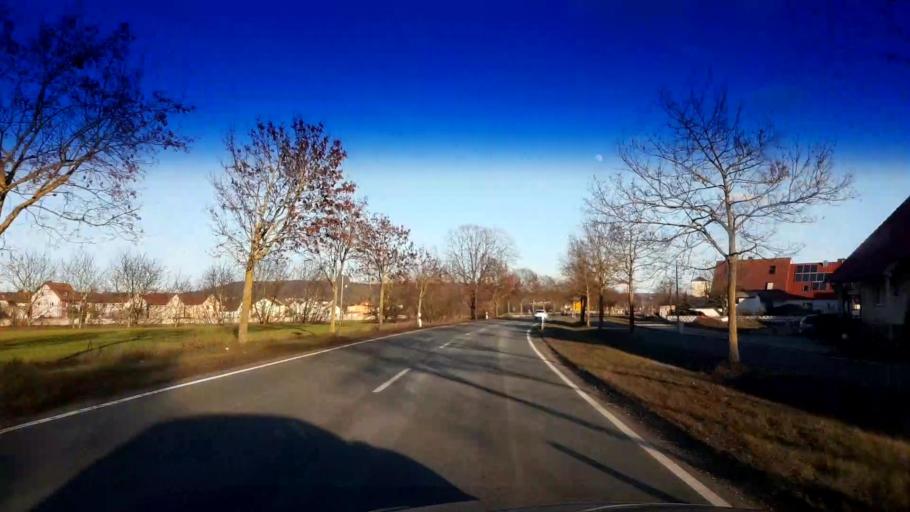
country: DE
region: Bavaria
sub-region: Upper Franconia
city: Hirschaid
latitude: 49.8100
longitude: 10.9760
